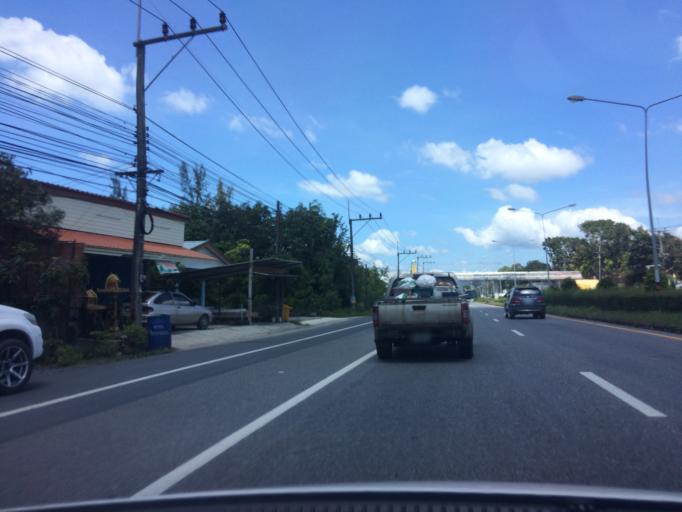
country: TH
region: Phangnga
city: Thai Mueang
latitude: 8.2206
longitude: 98.2981
